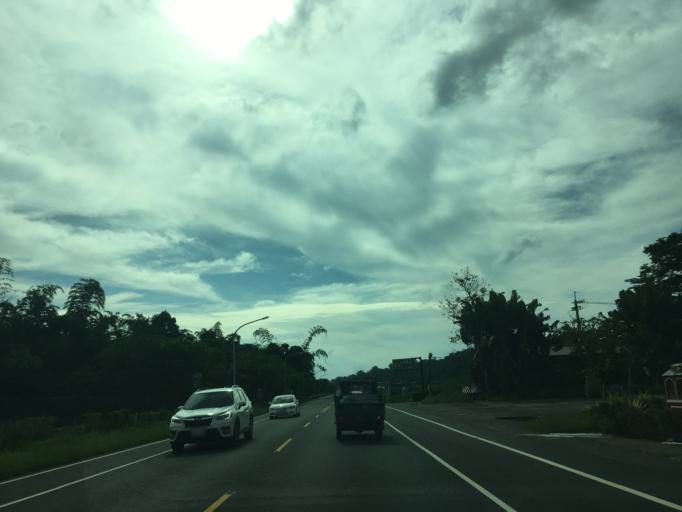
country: TW
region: Taiwan
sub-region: Chiayi
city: Jiayi Shi
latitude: 23.4480
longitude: 120.5778
